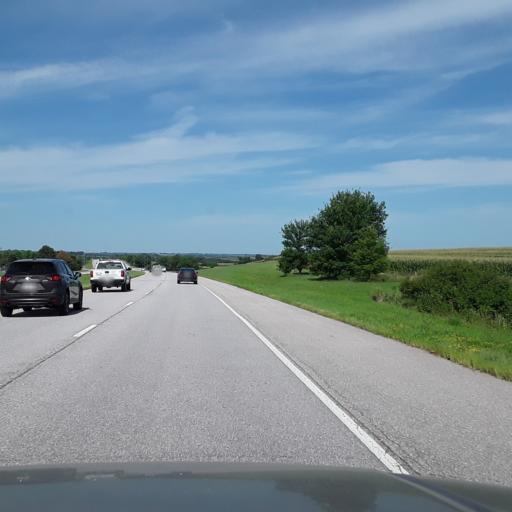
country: US
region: Nebraska
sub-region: Lancaster County
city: Lincoln
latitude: 40.8792
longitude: -96.7480
